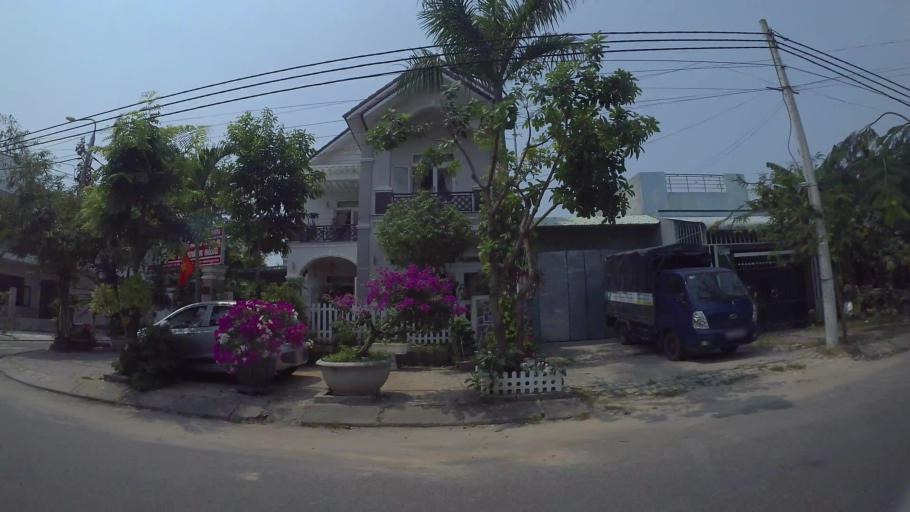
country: VN
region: Da Nang
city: Cam Le
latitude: 16.0029
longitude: 108.2180
